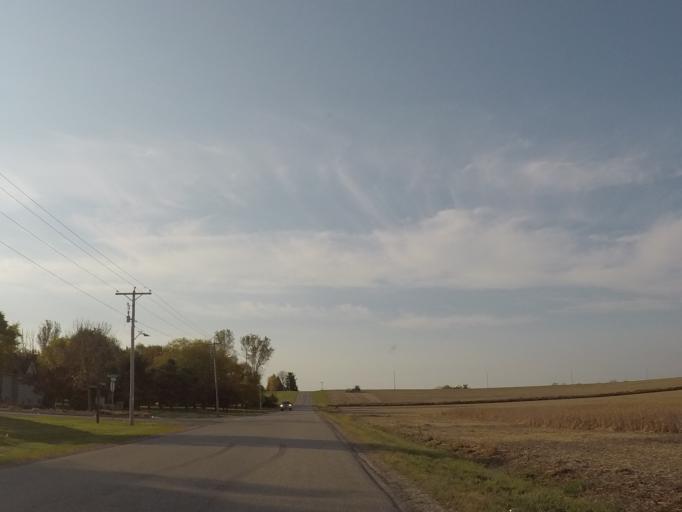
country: US
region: Wisconsin
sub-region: Dane County
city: Cross Plains
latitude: 43.0549
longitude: -89.6010
